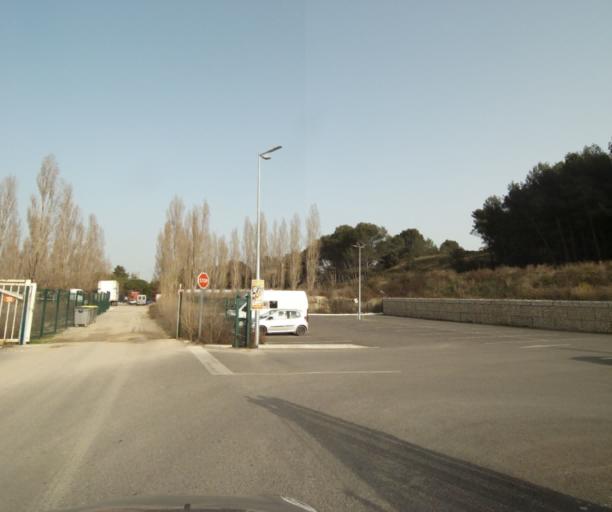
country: FR
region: Provence-Alpes-Cote d'Azur
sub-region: Departement des Bouches-du-Rhone
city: Septemes-les-Vallons
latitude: 43.4161
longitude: 5.3692
